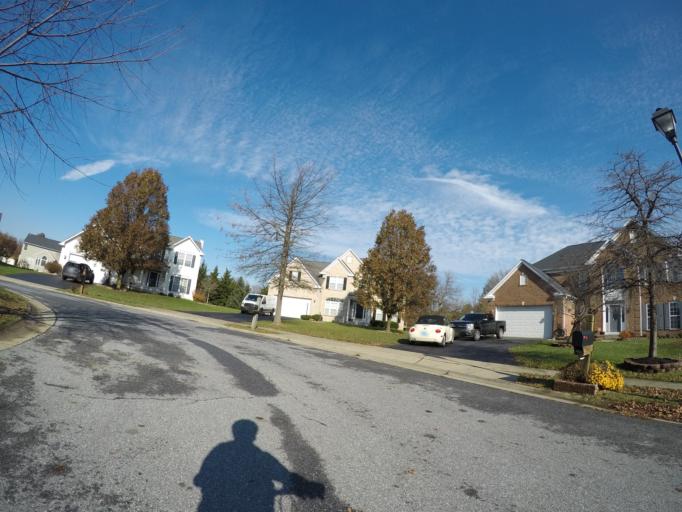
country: US
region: Maryland
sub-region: Frederick County
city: Ballenger Creek
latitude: 39.3725
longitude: -77.4380
